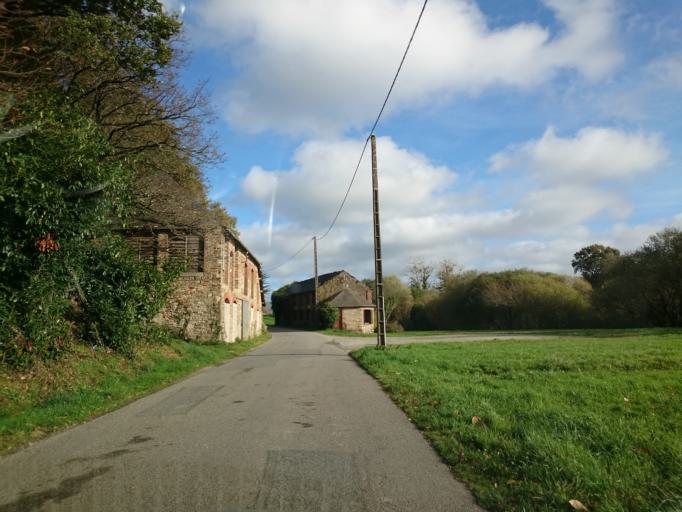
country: FR
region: Brittany
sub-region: Departement d'Ille-et-Vilaine
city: Bain-de-Bretagne
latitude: 47.8466
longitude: -1.6747
